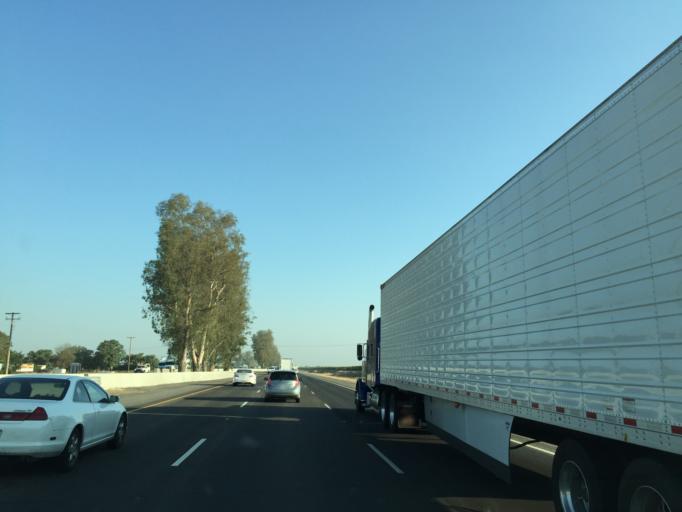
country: US
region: California
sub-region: Tulare County
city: London
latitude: 36.4717
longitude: -119.5007
